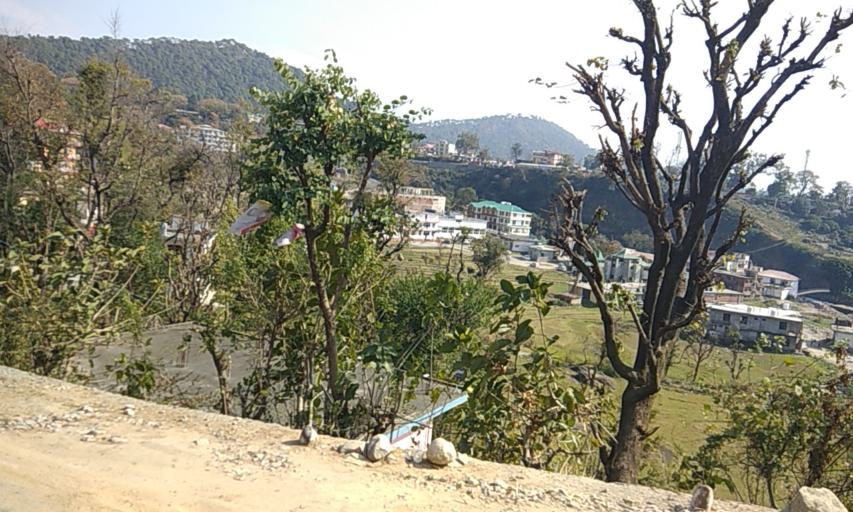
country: IN
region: Himachal Pradesh
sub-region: Kangra
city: Dharmsala
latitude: 32.1508
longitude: 76.4177
